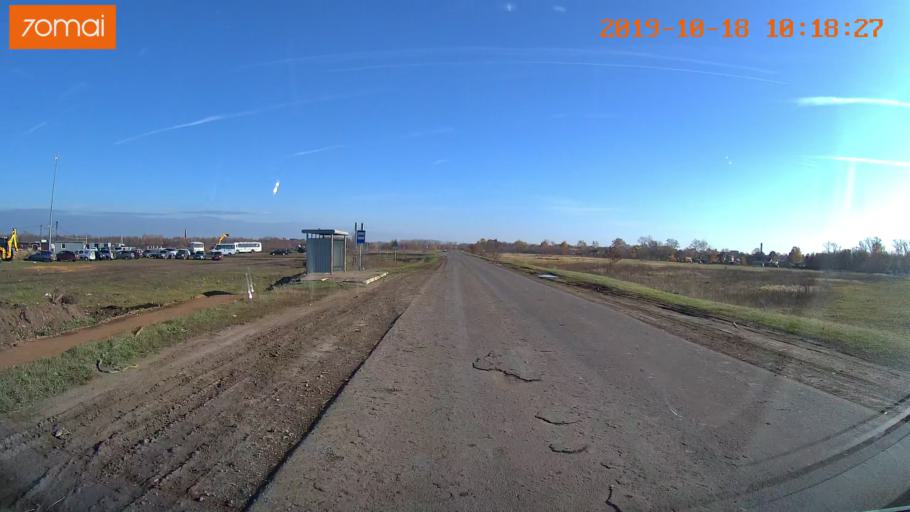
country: RU
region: Tula
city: Kurkino
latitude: 53.4172
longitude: 38.6326
